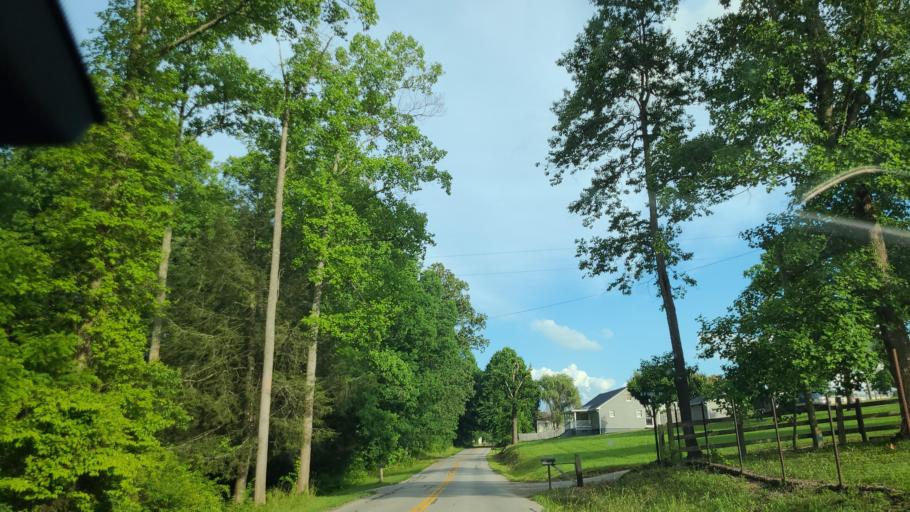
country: US
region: Kentucky
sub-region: Whitley County
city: Corbin
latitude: 36.9100
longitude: -84.2464
